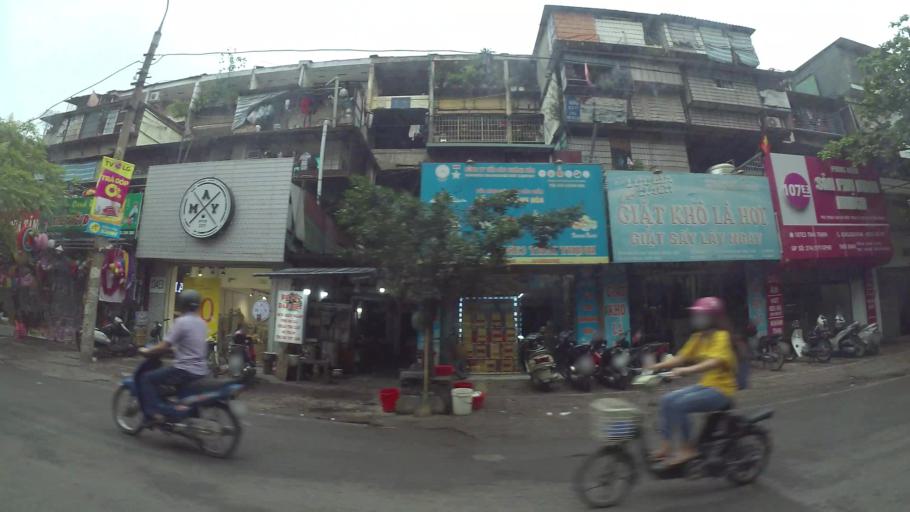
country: VN
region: Ha Noi
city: Dong Da
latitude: 21.0106
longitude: 105.8185
